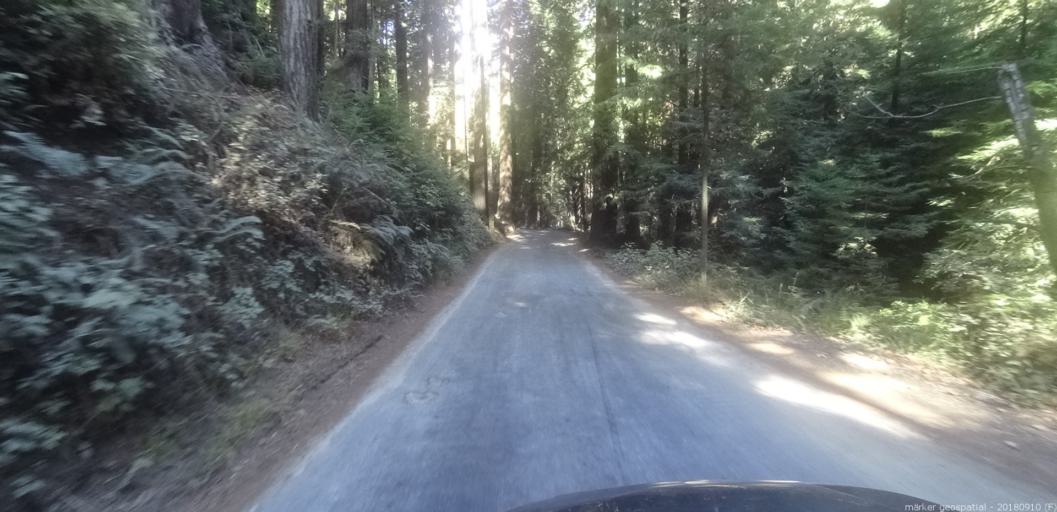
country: US
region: California
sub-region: Monterey County
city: Carmel Valley Village
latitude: 36.3972
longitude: -121.8830
